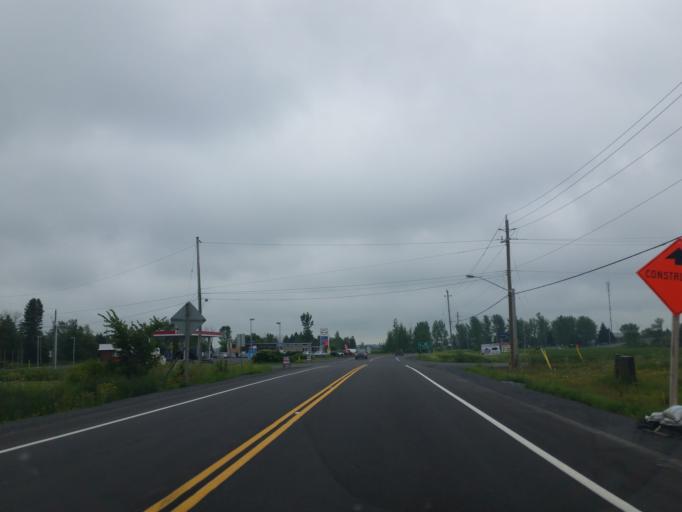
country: CA
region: Ontario
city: Clarence-Rockland
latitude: 45.3416
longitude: -75.3452
